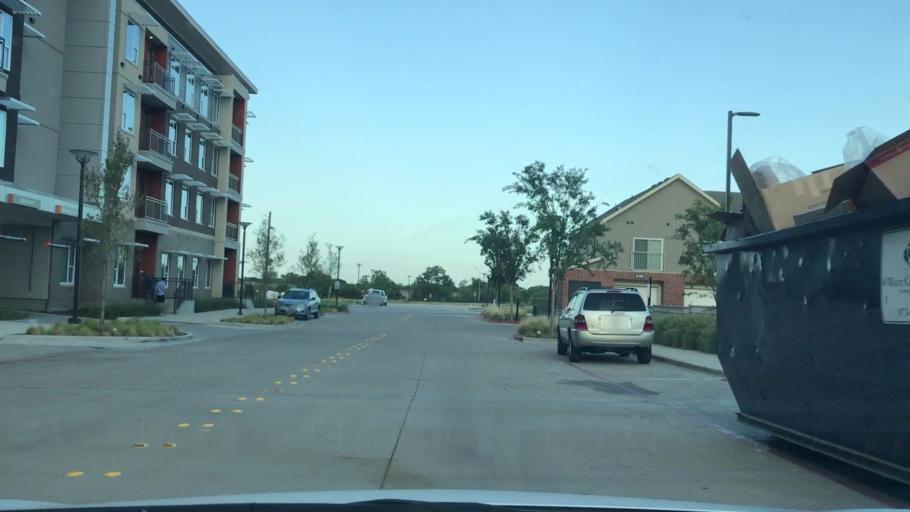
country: US
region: Texas
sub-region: Dallas County
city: Richardson
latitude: 32.9944
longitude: -96.7486
